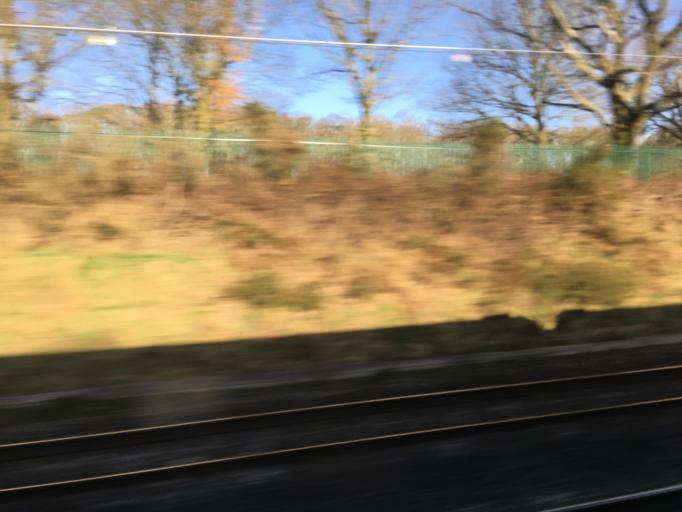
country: GB
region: England
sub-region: Wokingham
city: Charvil
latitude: 51.4660
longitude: -0.8930
